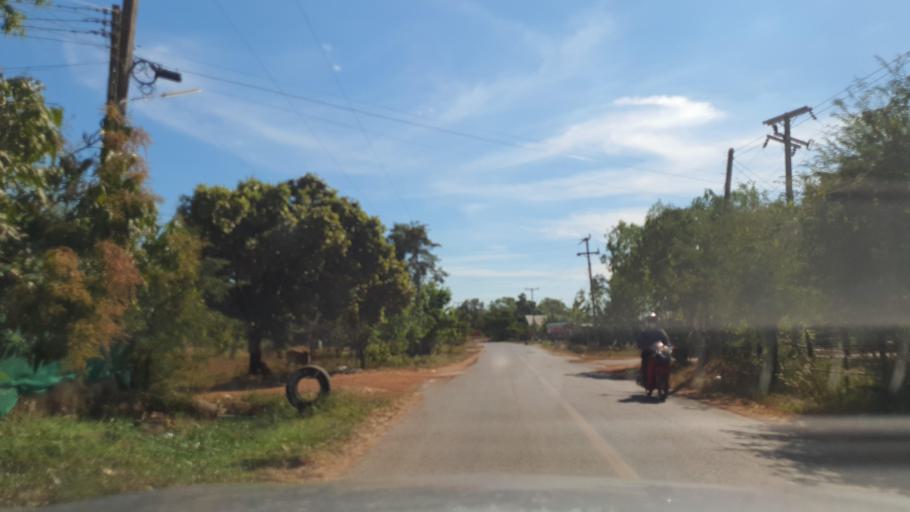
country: TH
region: Kalasin
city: Khao Wong
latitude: 16.6941
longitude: 104.1122
